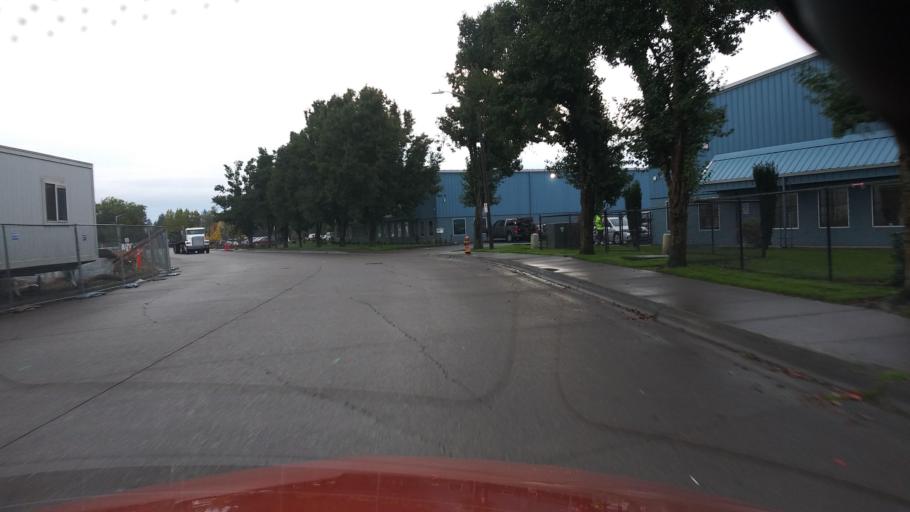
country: US
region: Oregon
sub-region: Washington County
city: Cornelius
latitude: 45.5266
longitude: -123.0626
